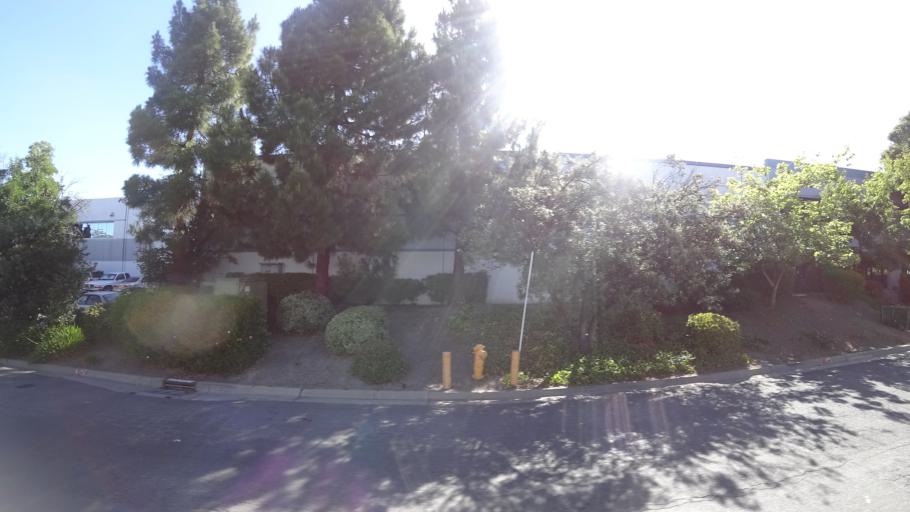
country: US
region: California
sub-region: Alameda County
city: Union City
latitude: 37.6187
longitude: -122.0501
